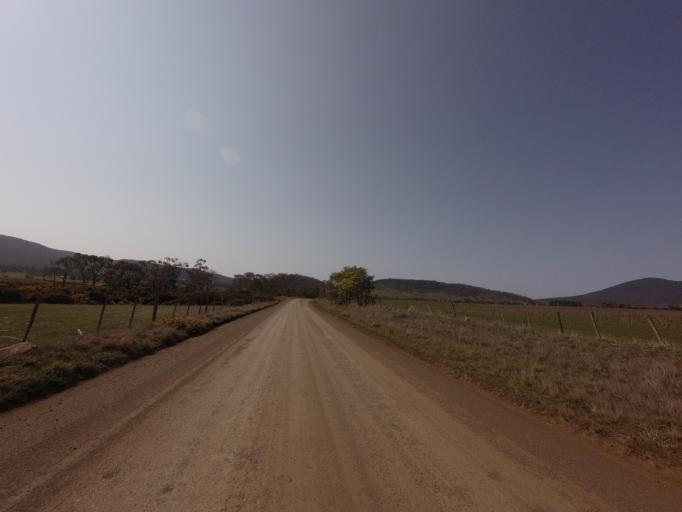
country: AU
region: Tasmania
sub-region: Break O'Day
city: St Helens
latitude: -41.8171
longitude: 147.9374
